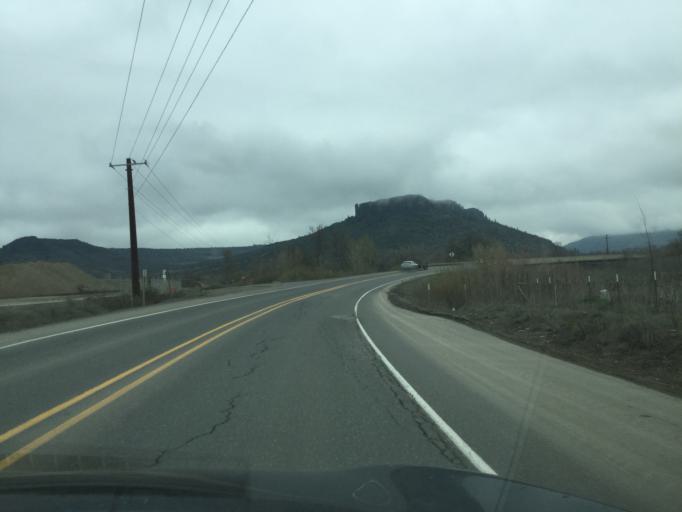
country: US
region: Oregon
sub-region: Jackson County
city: Central Point
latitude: 42.4247
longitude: -122.9587
